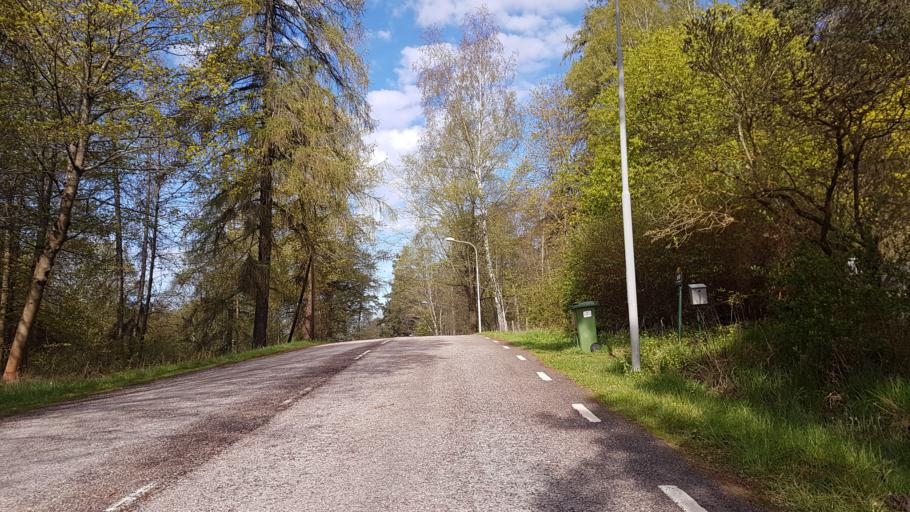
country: SE
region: Stockholm
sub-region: Stockholms Kommun
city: OEstermalm
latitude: 59.3561
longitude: 18.0689
